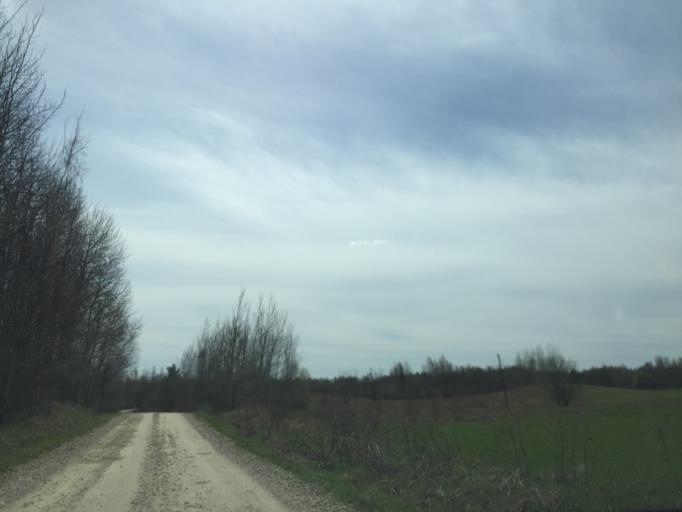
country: LV
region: Ludzas Rajons
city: Ludza
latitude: 56.5414
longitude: 27.5269
